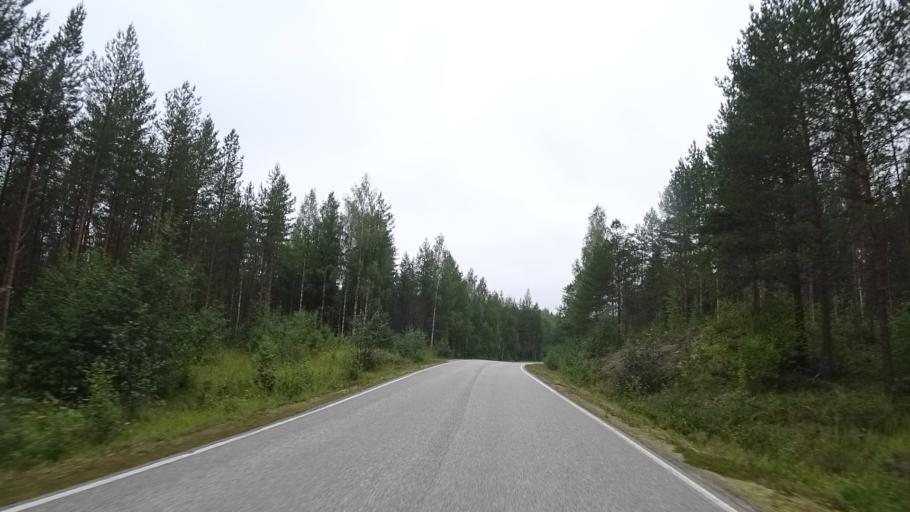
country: FI
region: North Karelia
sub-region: Pielisen Karjala
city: Lieksa
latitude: 63.3247
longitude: 30.2358
